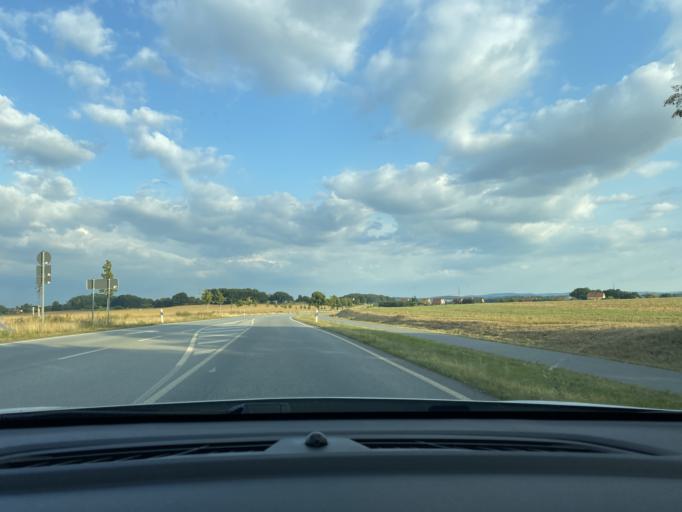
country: DE
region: Saxony
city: Neschwitz
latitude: 51.2550
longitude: 14.3518
